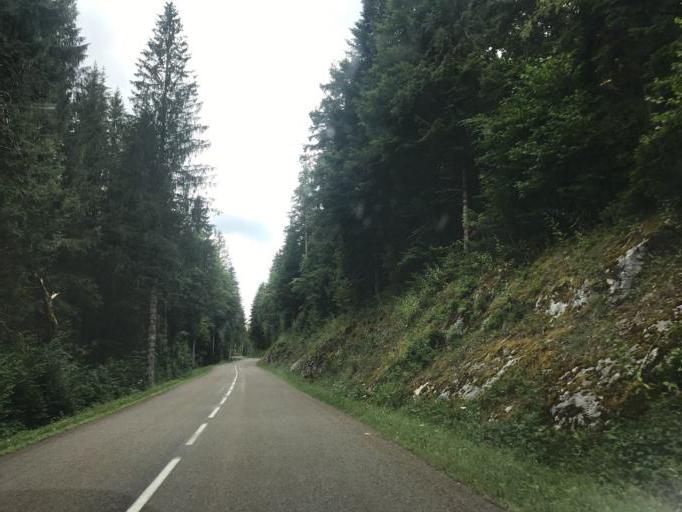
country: FR
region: Franche-Comte
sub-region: Departement du Jura
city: Valfin-les-Saint-Claude
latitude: 46.4936
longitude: 5.8490
